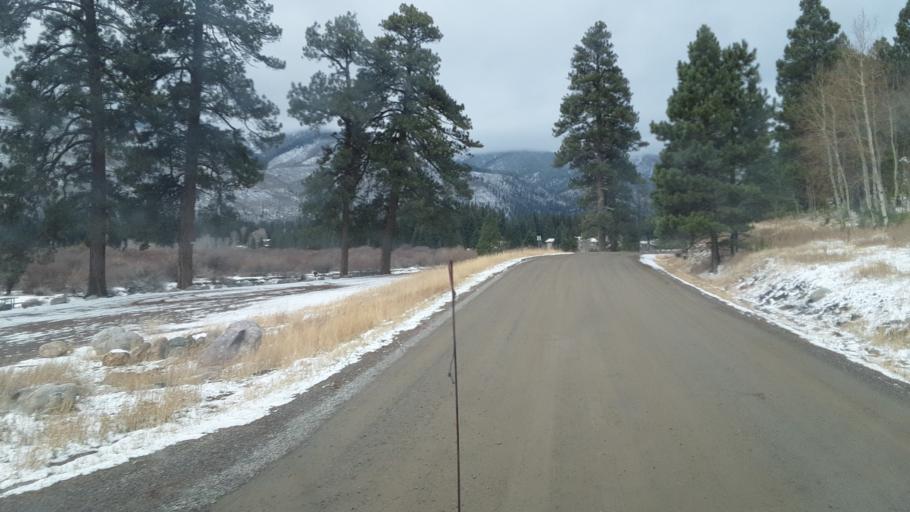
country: US
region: Colorado
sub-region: La Plata County
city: Bayfield
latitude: 37.4322
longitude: -107.5422
